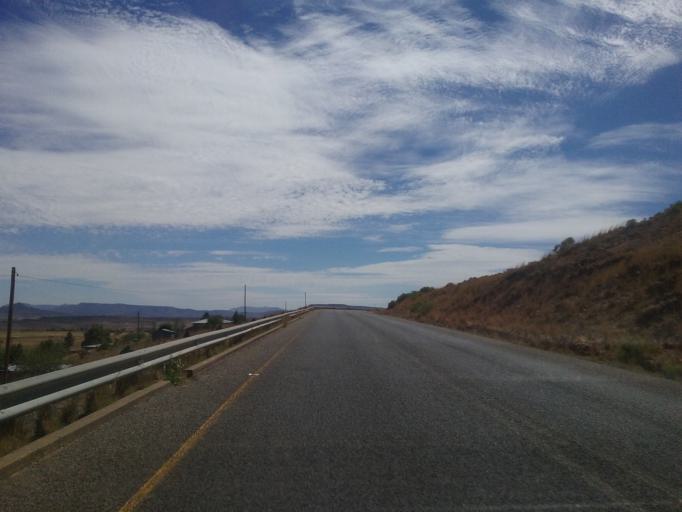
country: LS
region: Mohale's Hoek District
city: Mohale's Hoek
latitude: -30.1906
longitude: 27.4161
